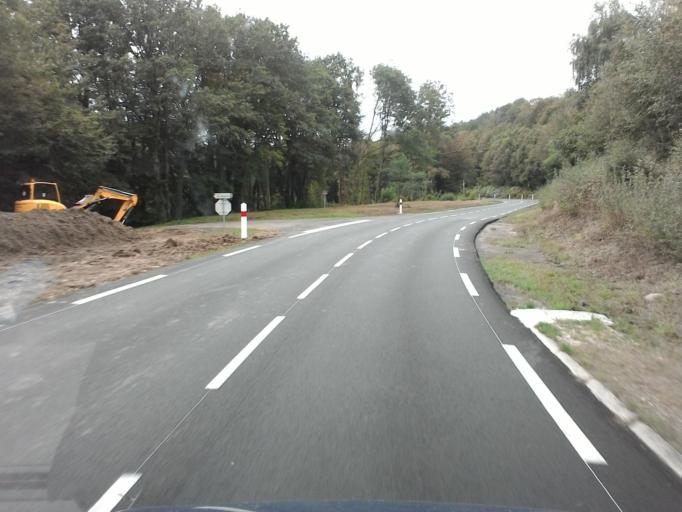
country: FR
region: Bourgogne
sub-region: Departement de Saone-et-Loire
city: Saint-Eusebe
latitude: 46.6060
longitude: 4.4784
